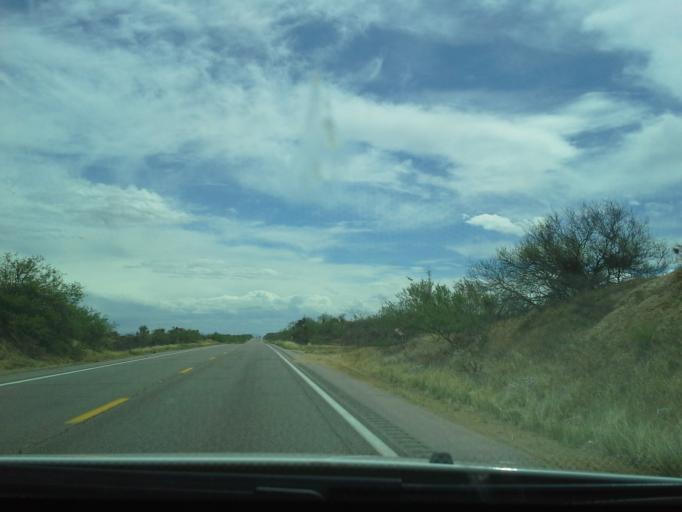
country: US
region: Arizona
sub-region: Gila County
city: Peridot
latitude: 33.3350
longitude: -110.5830
